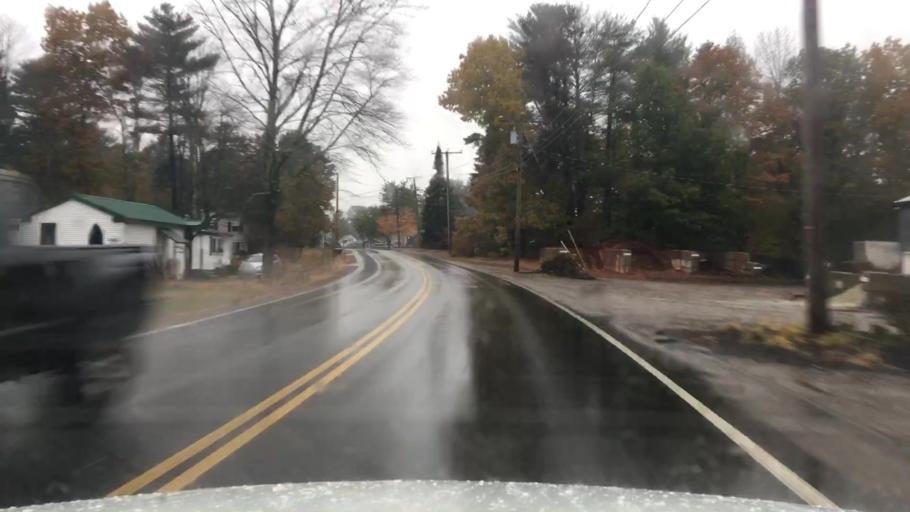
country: US
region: New Hampshire
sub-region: Strafford County
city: Rochester
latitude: 43.3417
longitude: -70.9653
